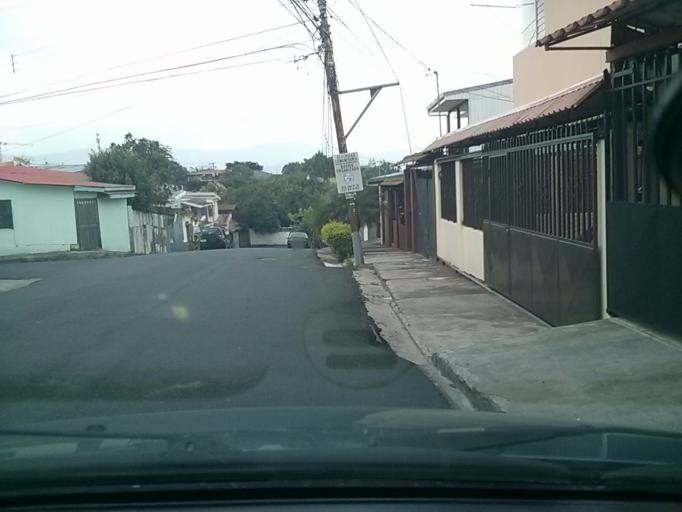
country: CR
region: San Jose
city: Sabanilla
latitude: 9.9362
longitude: -84.0413
